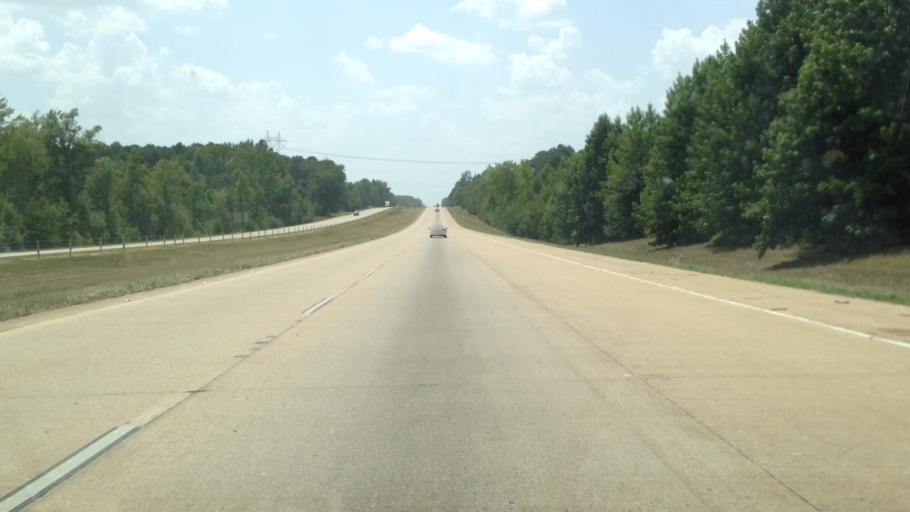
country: US
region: Louisiana
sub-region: Lincoln Parish
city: Grambling
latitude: 32.5422
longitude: -92.7179
